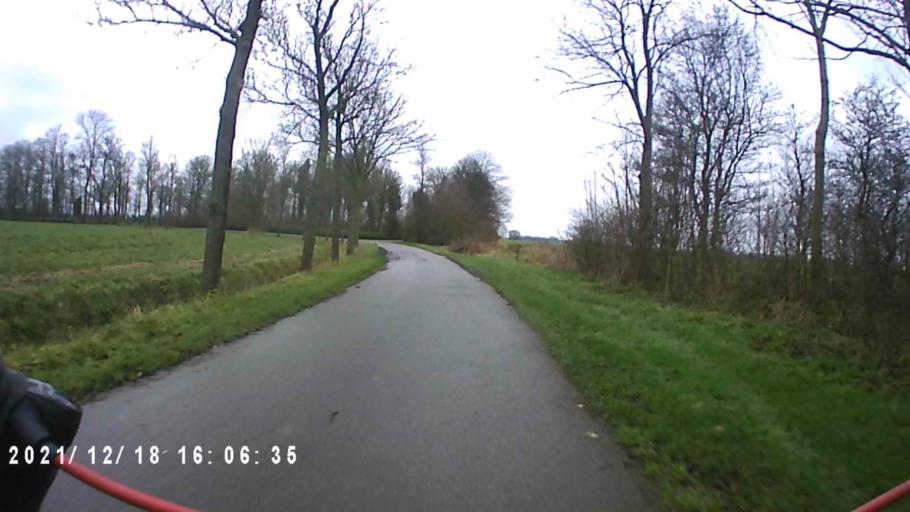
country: NL
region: Friesland
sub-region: Gemeente Dongeradeel
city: Anjum
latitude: 53.3568
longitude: 6.0776
